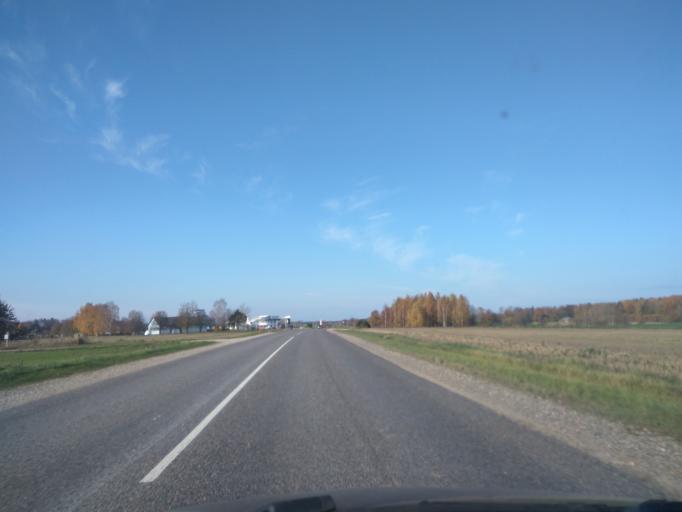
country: LV
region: Kuldigas Rajons
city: Kuldiga
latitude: 56.9957
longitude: 21.9044
